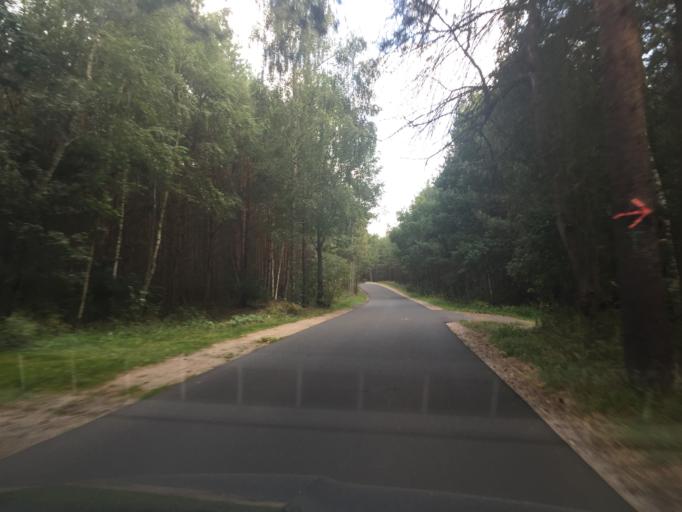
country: DE
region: Brandenburg
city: Grunheide
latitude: 52.3633
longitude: 13.7883
